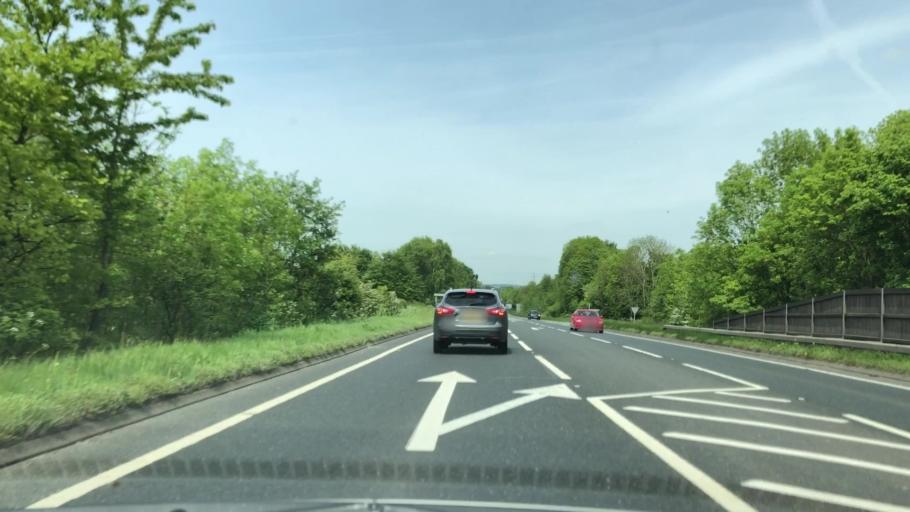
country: GB
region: England
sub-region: Shropshire
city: Gobowen
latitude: 52.9011
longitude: -3.0437
